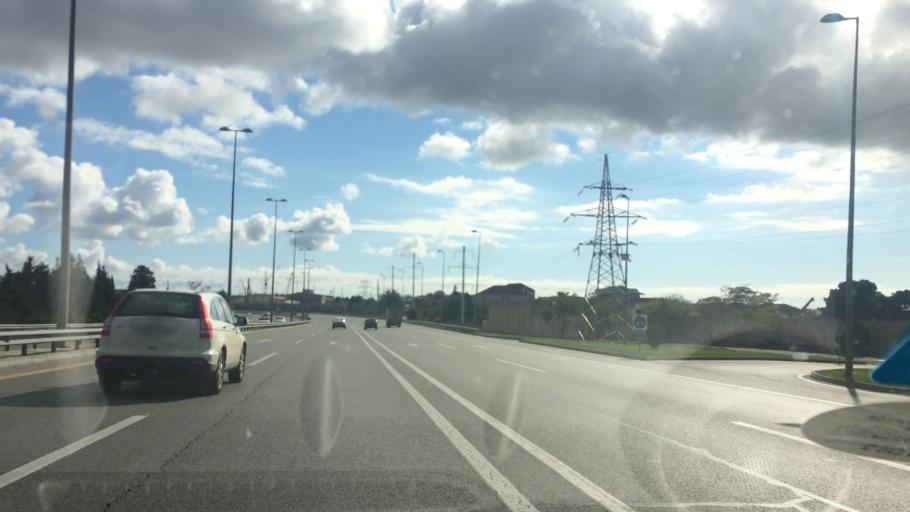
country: AZ
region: Baki
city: Ramana
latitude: 40.4398
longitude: 49.9744
